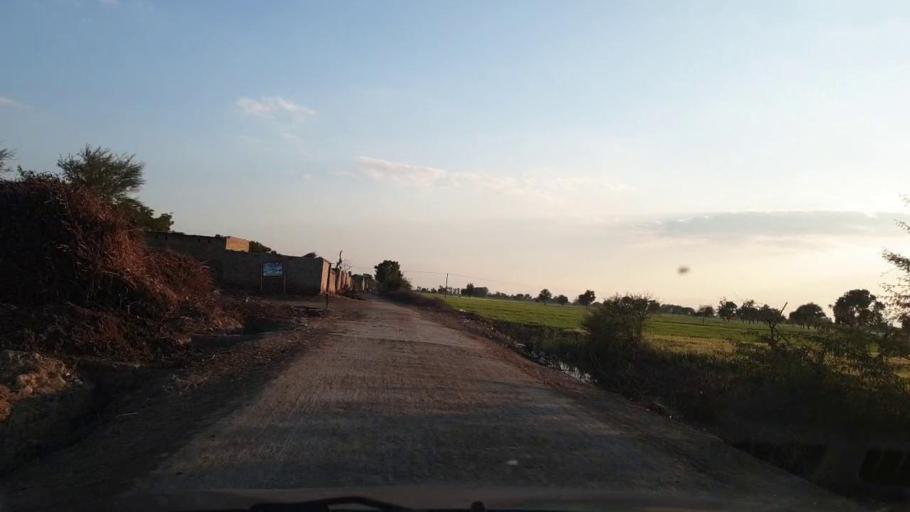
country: PK
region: Sindh
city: Sinjhoro
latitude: 25.9976
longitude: 68.8014
